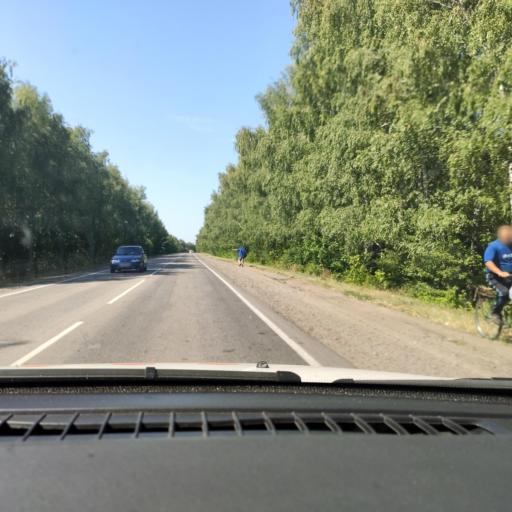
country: RU
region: Voronezj
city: Imeni Pervogo Maya
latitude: 50.7350
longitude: 39.3910
